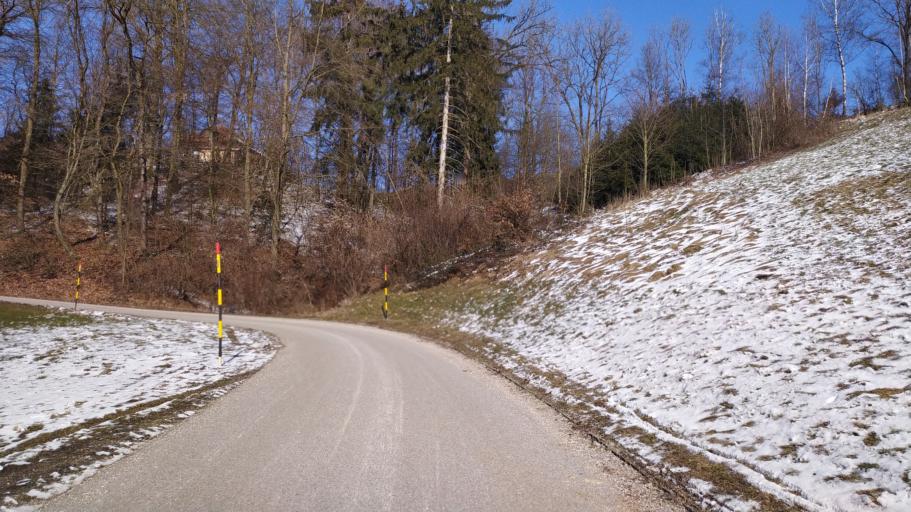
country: AT
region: Upper Austria
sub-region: Politischer Bezirk Urfahr-Umgebung
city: Ottensheim
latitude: 48.3358
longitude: 14.2073
